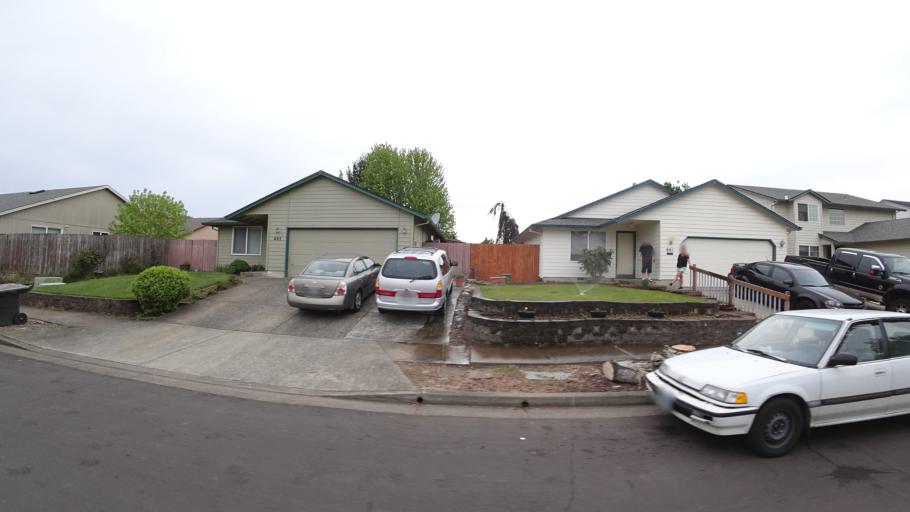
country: US
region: Oregon
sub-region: Washington County
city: Aloha
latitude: 45.5146
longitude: -122.9052
